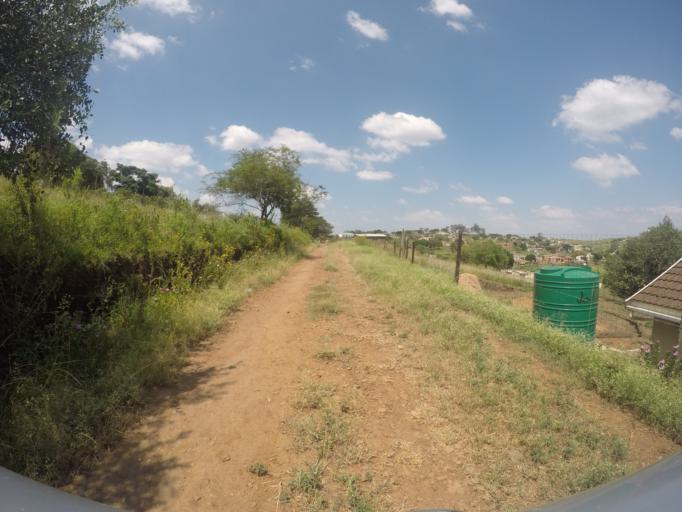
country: ZA
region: KwaZulu-Natal
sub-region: uThungulu District Municipality
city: Empangeni
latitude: -28.6002
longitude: 31.7395
